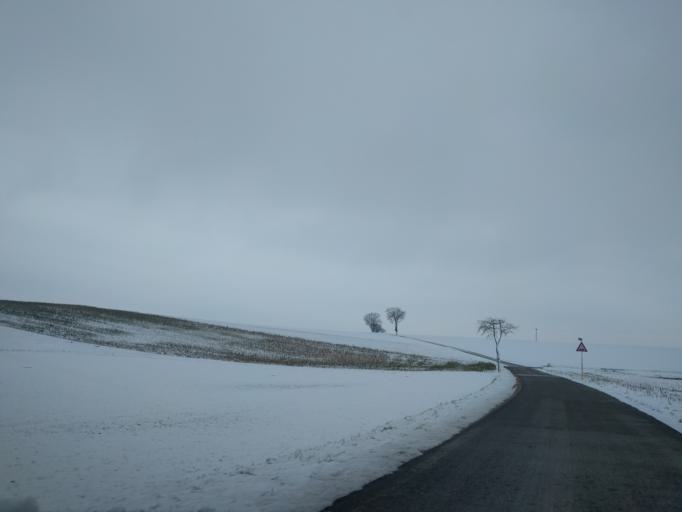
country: DE
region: Bavaria
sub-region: Swabia
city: Donauwoerth
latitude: 48.7029
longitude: 10.7355
